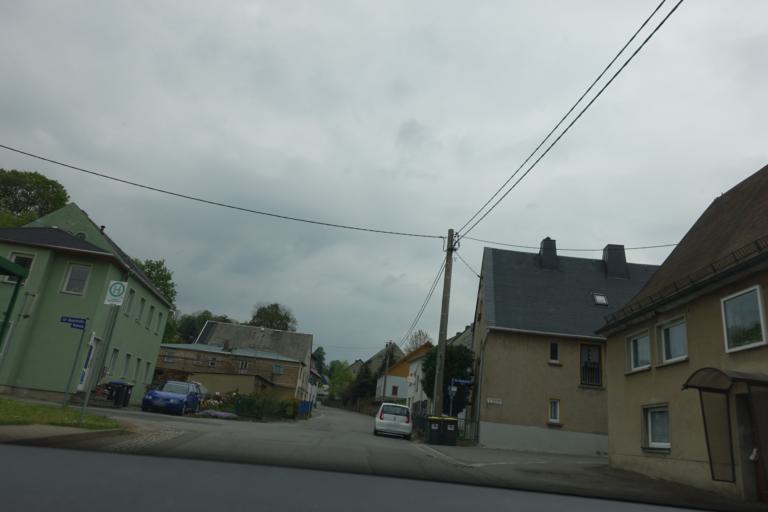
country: DE
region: Saxony
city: Leubsdorf
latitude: 50.7992
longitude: 13.1535
